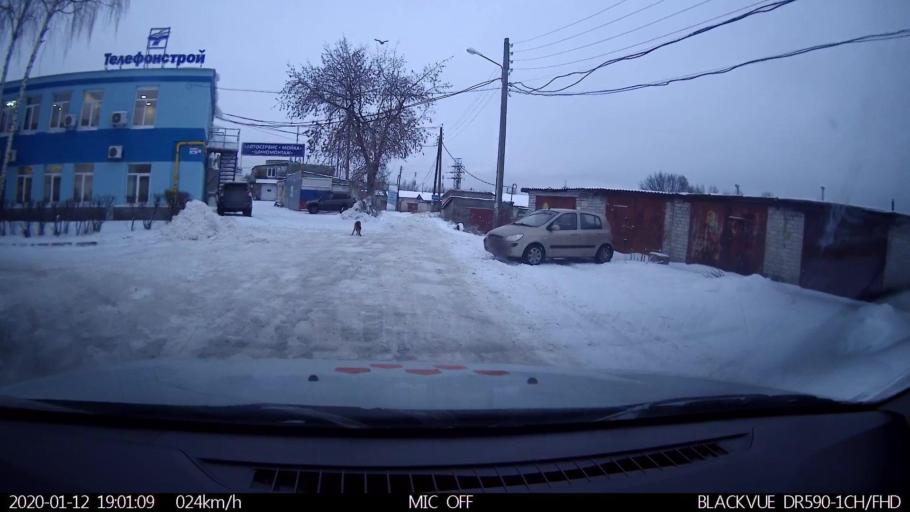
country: RU
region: Nizjnij Novgorod
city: Nizhniy Novgorod
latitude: 56.3316
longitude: 43.9089
